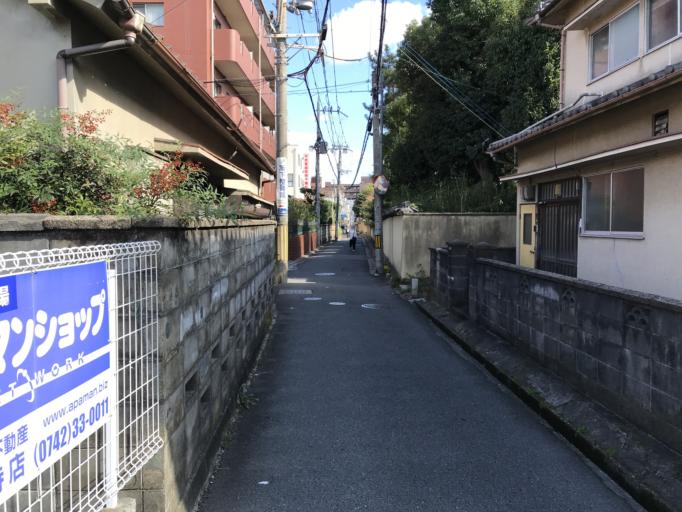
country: JP
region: Nara
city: Nara-shi
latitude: 34.6940
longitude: 135.7782
